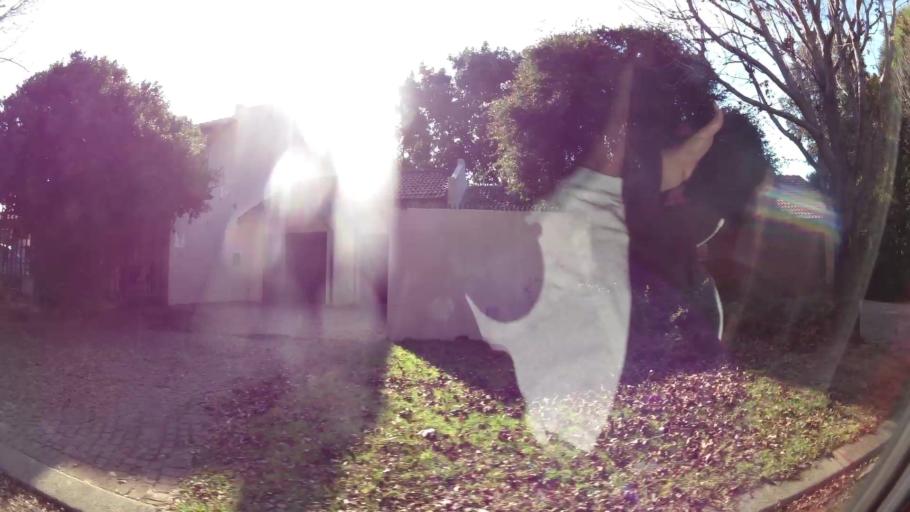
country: ZA
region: Gauteng
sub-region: City of Johannesburg Metropolitan Municipality
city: Roodepoort
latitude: -26.0965
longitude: 27.9450
